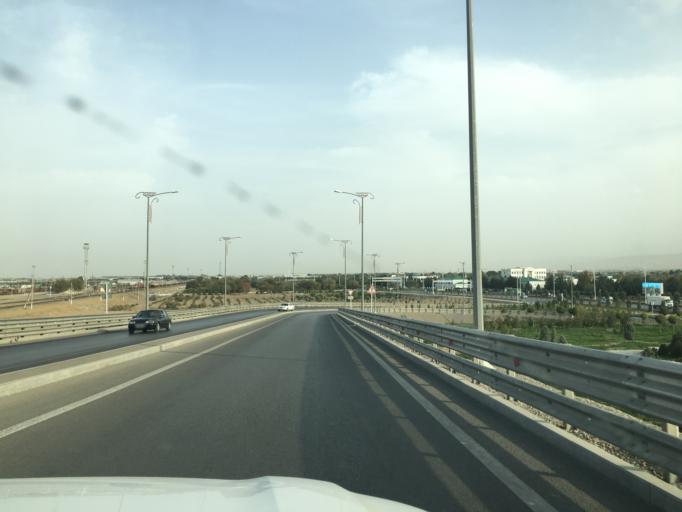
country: TM
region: Ahal
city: Annau
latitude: 37.9135
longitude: 58.4861
